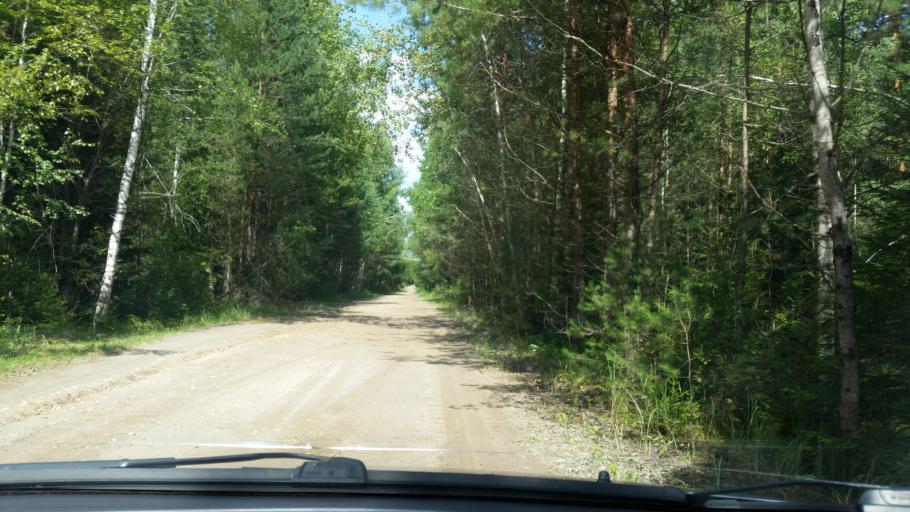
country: RU
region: Moskovskaya
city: Pushchino
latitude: 54.9151
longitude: 37.6856
